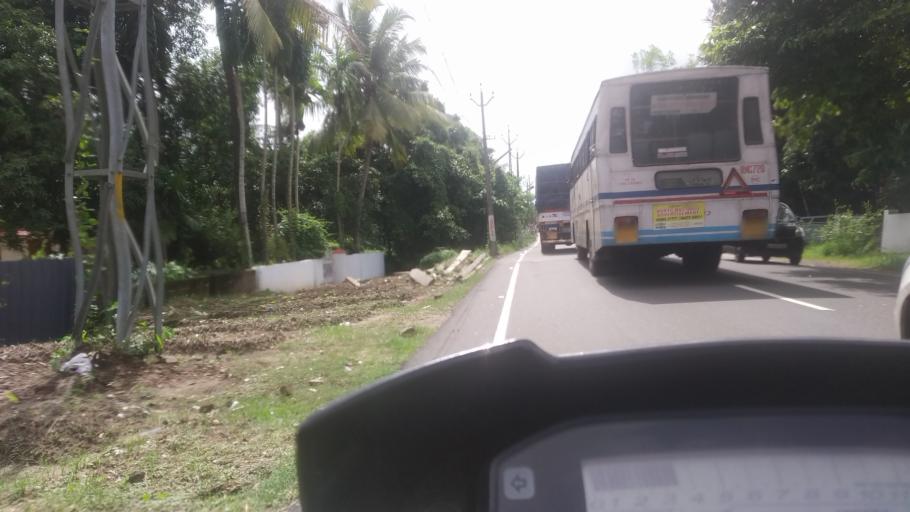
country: IN
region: Kerala
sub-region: Ernakulam
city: Elur
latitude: 10.1336
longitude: 76.2746
